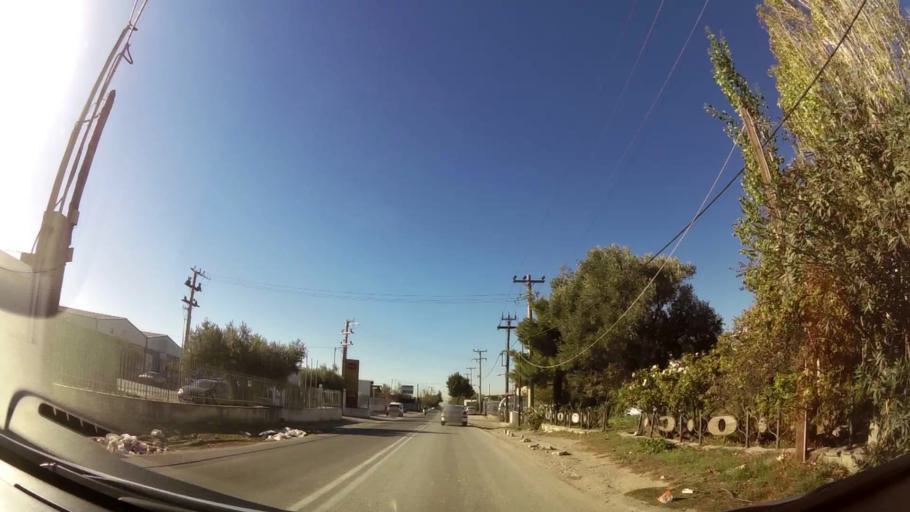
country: GR
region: Attica
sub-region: Nomarchia Athinas
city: Metamorfosi
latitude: 38.0818
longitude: 23.7654
